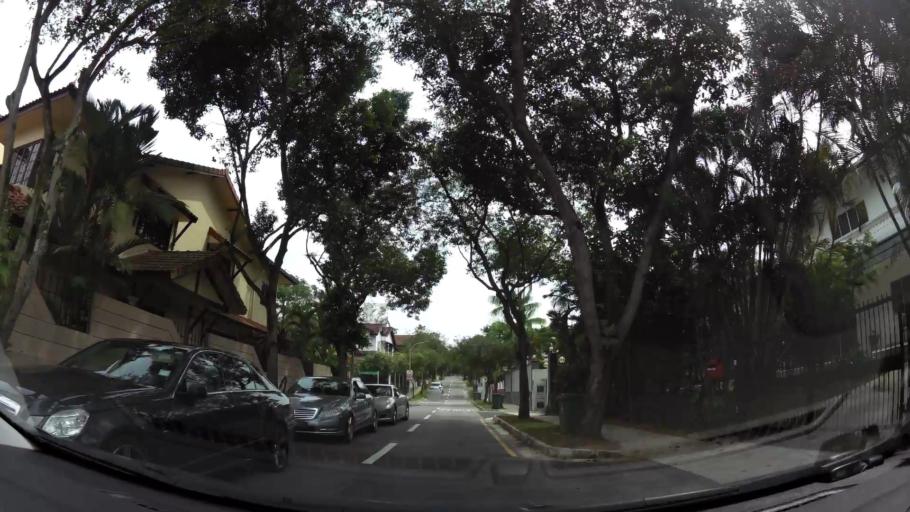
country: SG
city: Singapore
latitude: 1.3214
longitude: 103.7867
